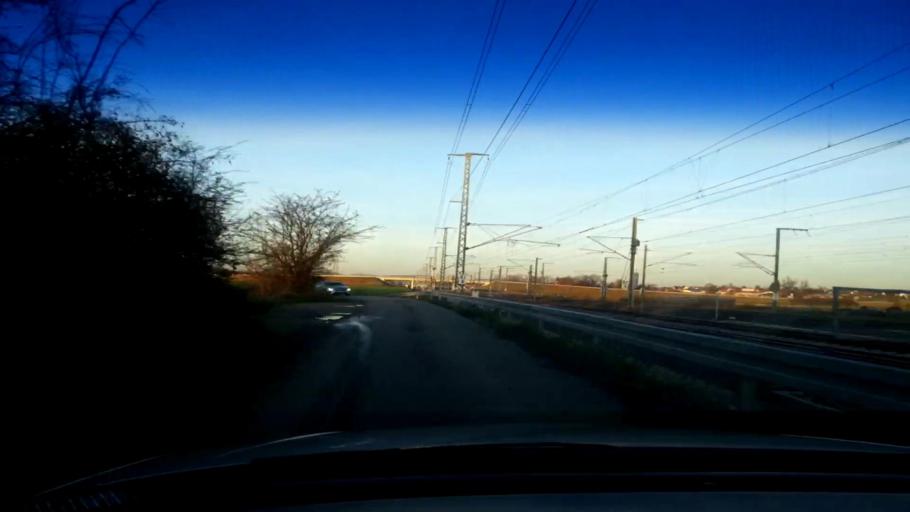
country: DE
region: Bavaria
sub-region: Upper Franconia
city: Ebensfeld
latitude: 50.0561
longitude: 10.9497
